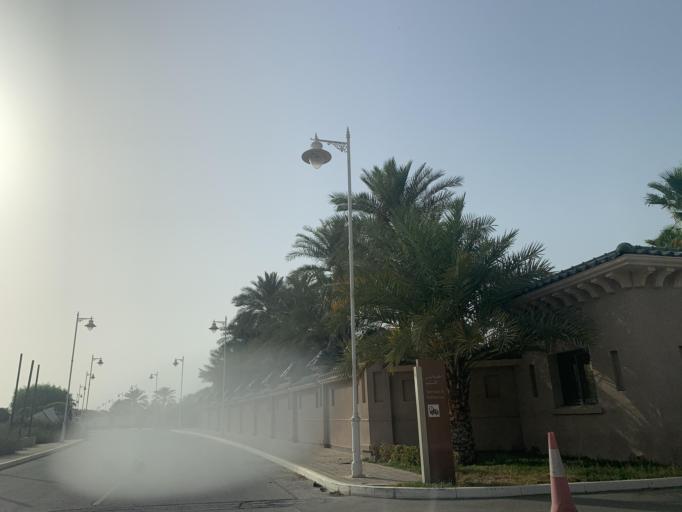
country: BH
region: Manama
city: Jidd Hafs
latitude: 26.2416
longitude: 50.5408
